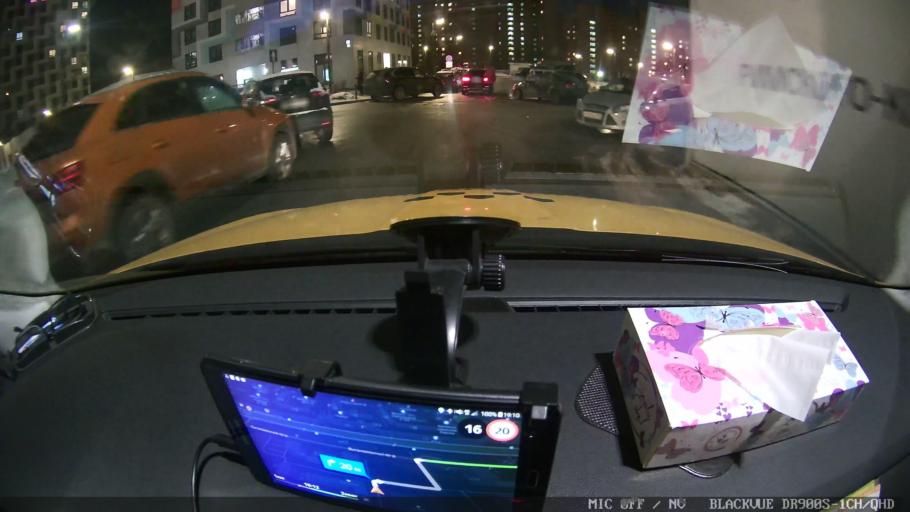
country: RU
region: Moscow
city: Bibirevo
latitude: 55.8752
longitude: 37.6017
